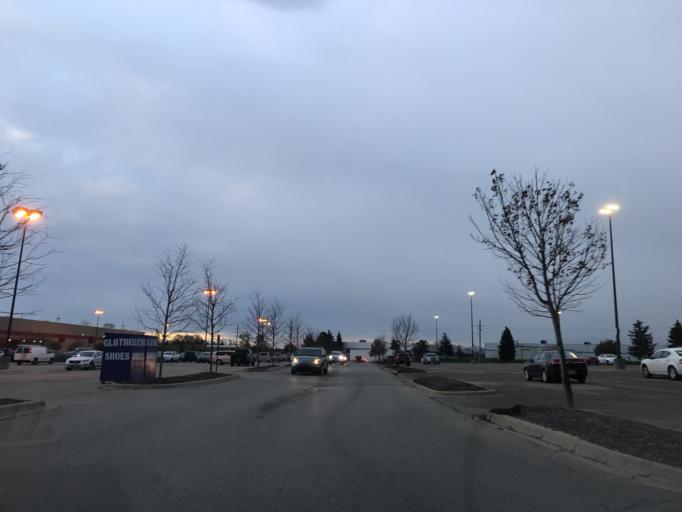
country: US
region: Michigan
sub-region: Wayne County
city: Northville
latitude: 42.4335
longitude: -83.4321
